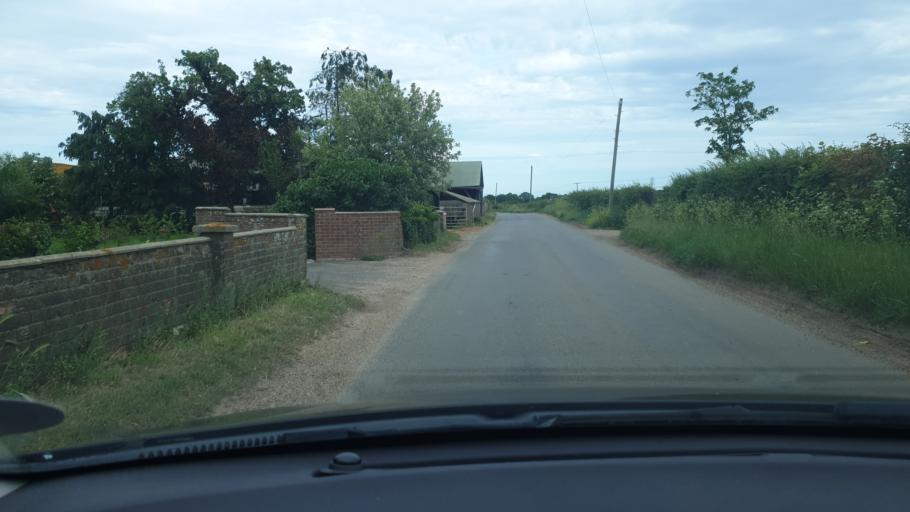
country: GB
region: England
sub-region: Essex
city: Great Bentley
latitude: 51.8898
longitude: 1.0850
